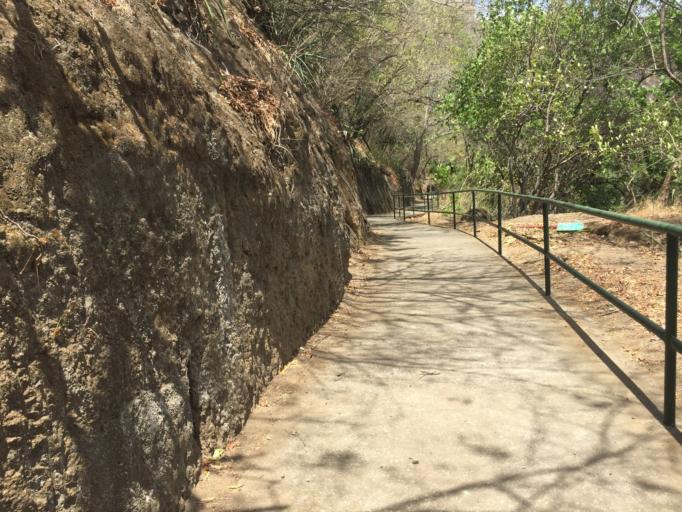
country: NI
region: Managua
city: Managua
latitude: 12.1388
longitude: -86.2725
